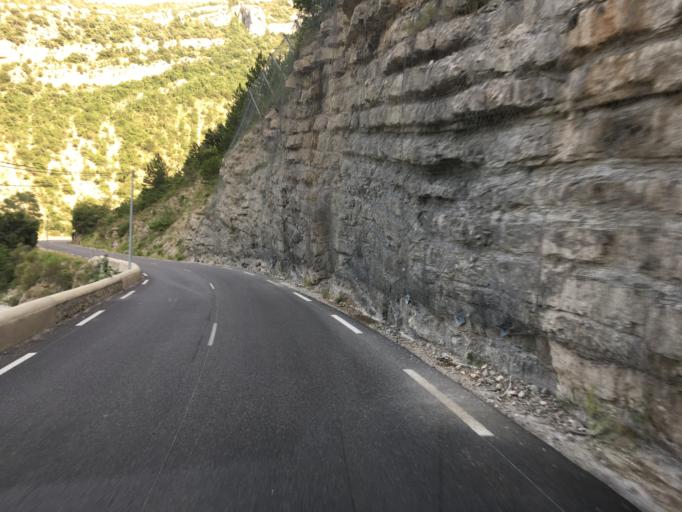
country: FR
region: Rhone-Alpes
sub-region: Departement de la Drome
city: Buis-les-Baronnies
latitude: 44.4287
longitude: 5.2772
